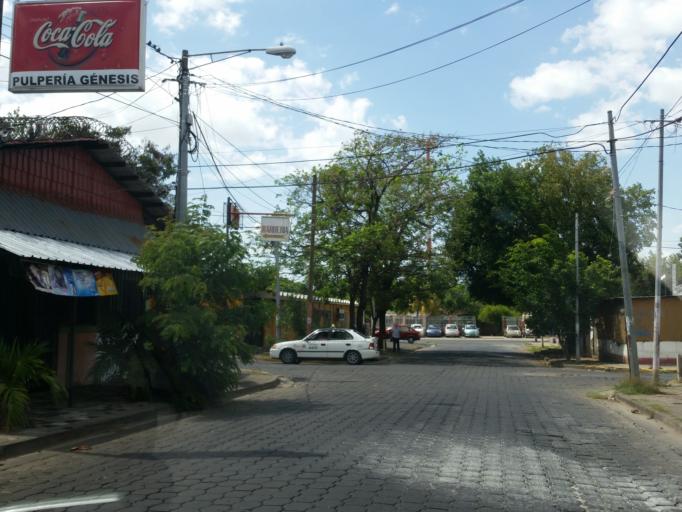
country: NI
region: Managua
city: Managua
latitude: 12.1403
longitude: -86.2414
